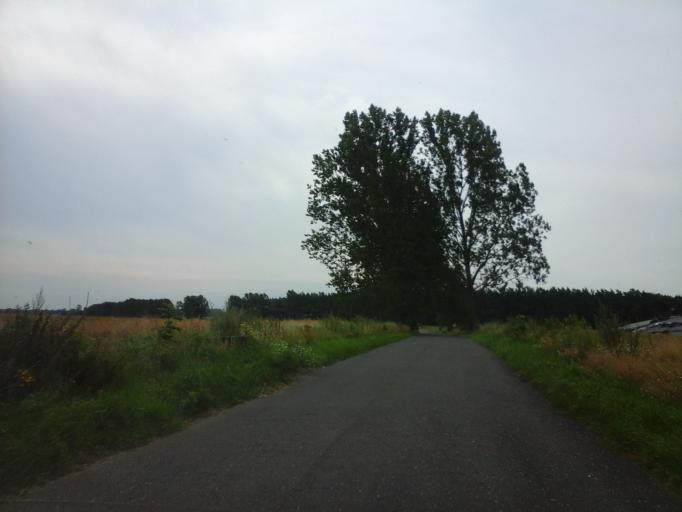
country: PL
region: West Pomeranian Voivodeship
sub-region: Powiat choszczenski
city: Recz
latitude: 53.2030
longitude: 15.5558
